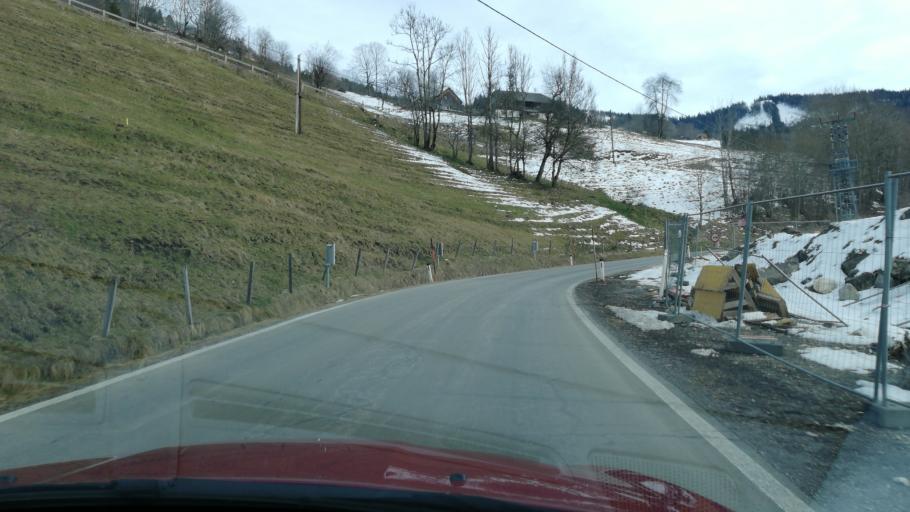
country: AT
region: Styria
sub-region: Politischer Bezirk Liezen
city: Donnersbach
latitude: 47.4573
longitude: 14.1394
